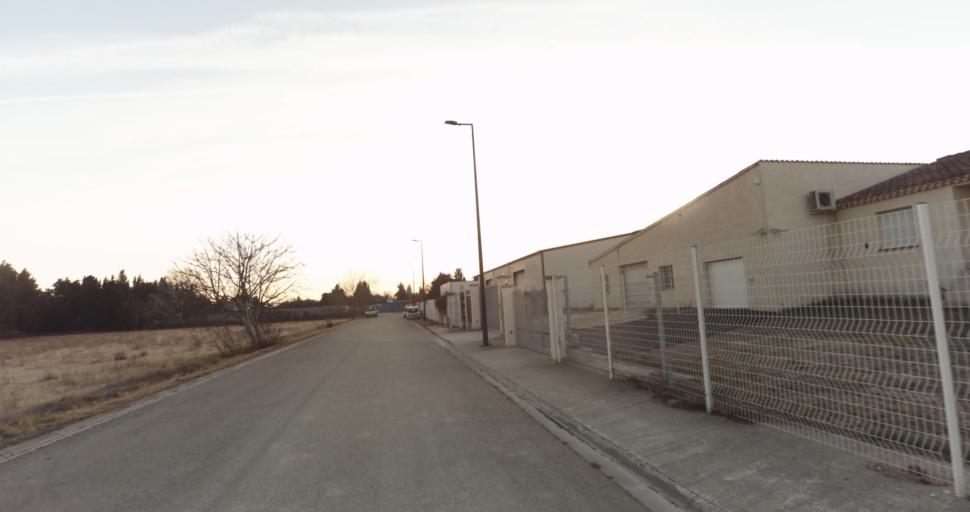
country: FR
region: Provence-Alpes-Cote d'Azur
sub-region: Departement des Bouches-du-Rhone
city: Barbentane
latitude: 43.9067
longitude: 4.7663
